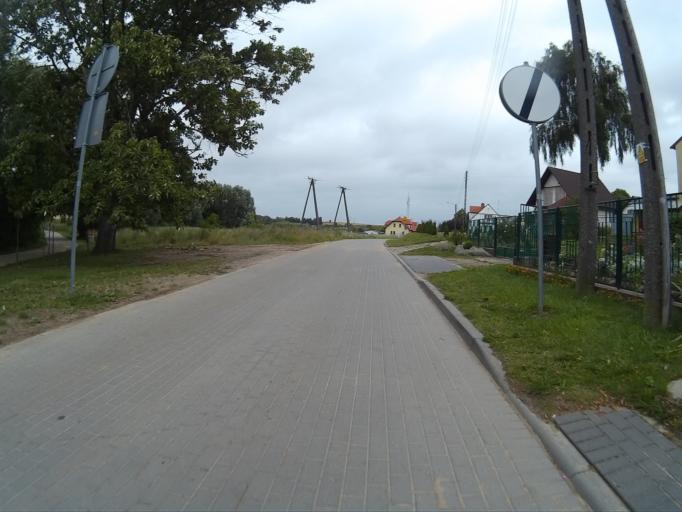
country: PL
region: Kujawsko-Pomorskie
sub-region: Powiat tucholski
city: Tuchola
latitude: 53.5902
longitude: 17.8788
